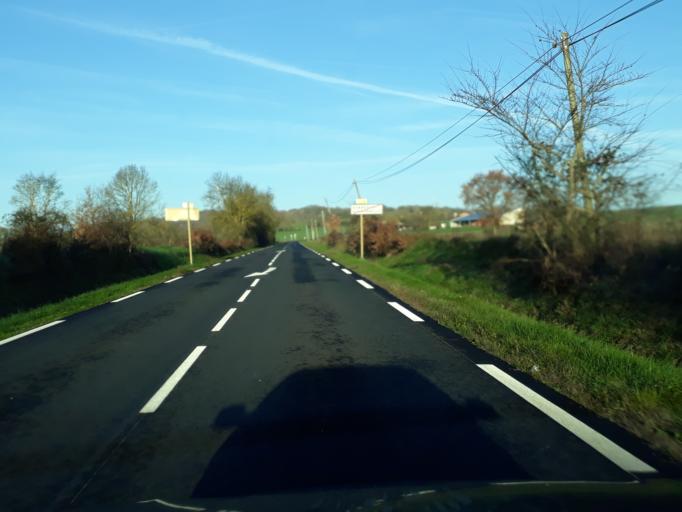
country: FR
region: Midi-Pyrenees
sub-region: Departement du Gers
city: Pujaudran
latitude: 43.5503
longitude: 1.1479
